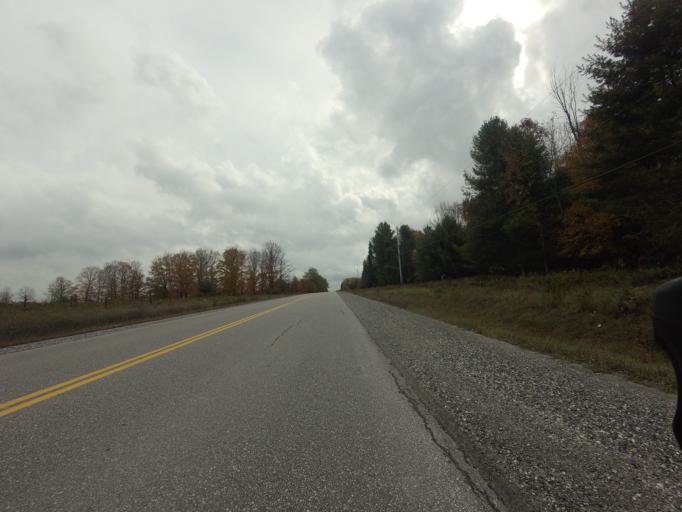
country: CA
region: Ontario
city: Perth
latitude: 45.0991
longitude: -76.4673
